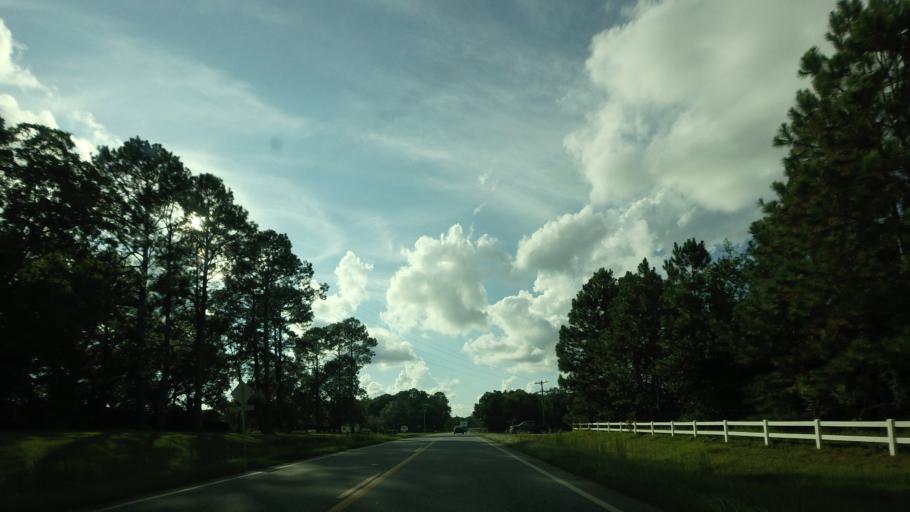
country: US
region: Georgia
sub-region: Pulaski County
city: Hawkinsville
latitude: 32.2883
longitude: -83.4942
